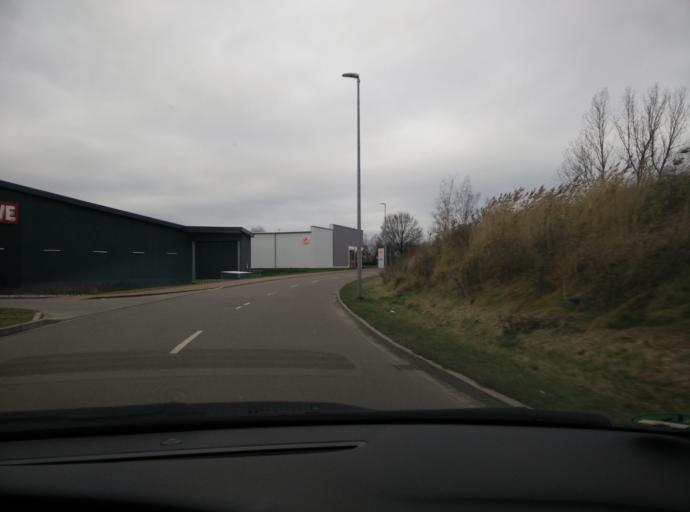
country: DE
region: Saxony
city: Bad Lausick
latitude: 51.1409
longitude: 12.6559
